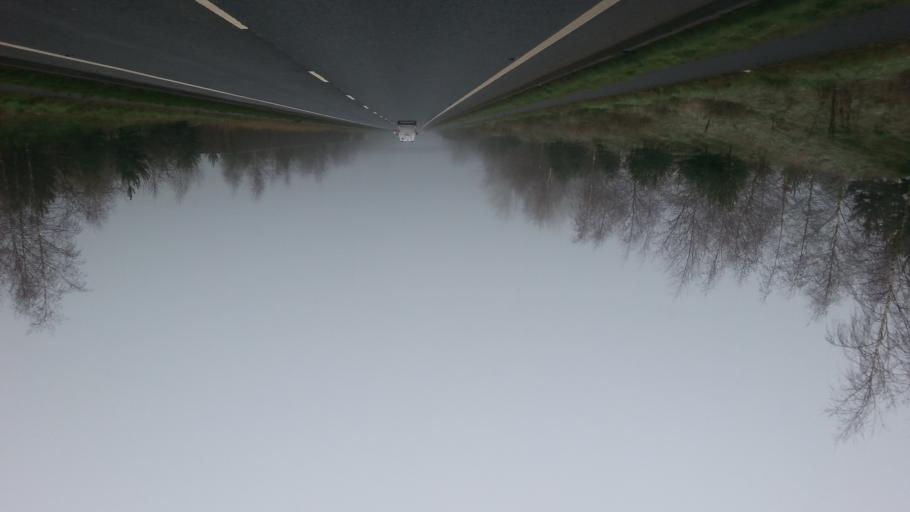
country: GB
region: England
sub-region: Cheshire East
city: Alderley Edge
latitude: 53.2765
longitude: -2.2420
